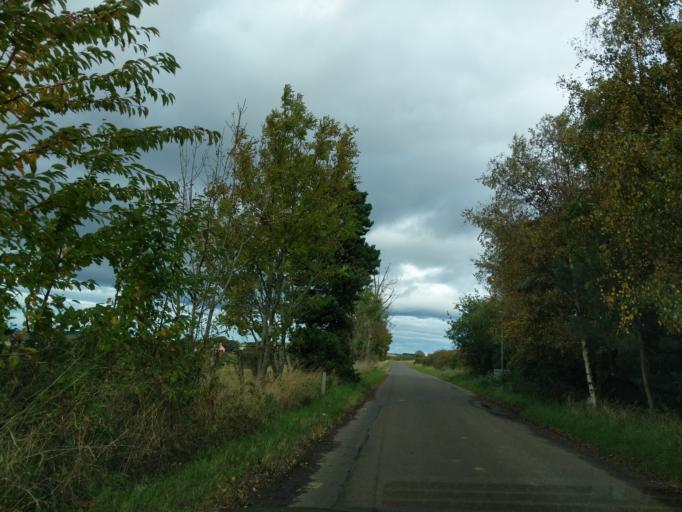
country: GB
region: Scotland
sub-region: East Lothian
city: Haddington
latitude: 55.9377
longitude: -2.7169
